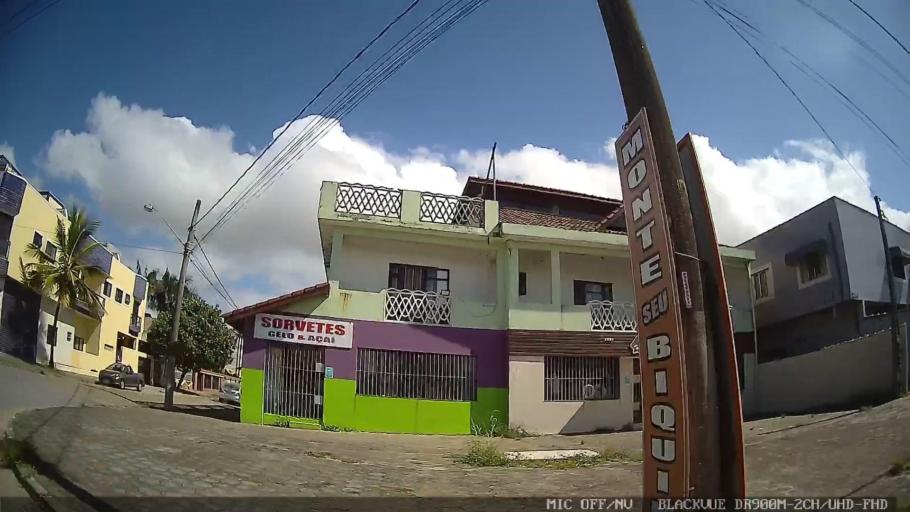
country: BR
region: Sao Paulo
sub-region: Peruibe
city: Peruibe
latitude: -24.3130
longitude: -46.9833
